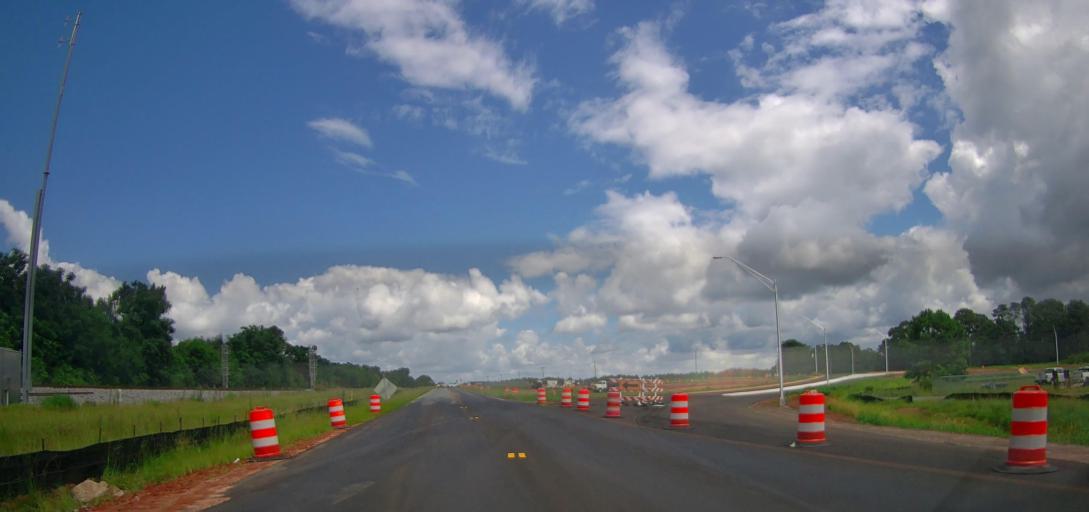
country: US
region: Georgia
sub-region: Houston County
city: Perry
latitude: 32.4653
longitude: -83.6175
